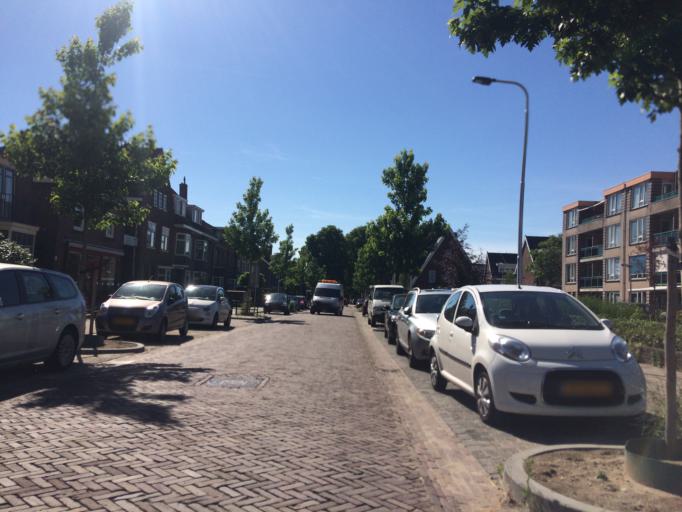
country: NL
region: Gelderland
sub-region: Gemeente Nijmegen
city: Nijmegen
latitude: 51.8327
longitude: 5.8537
